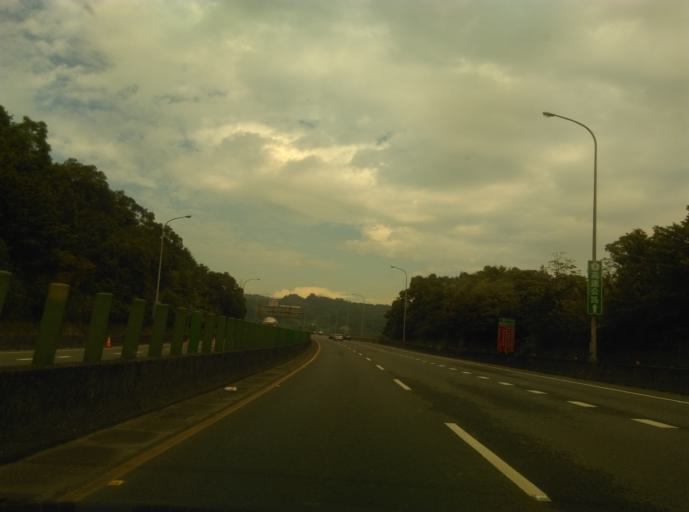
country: TW
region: Taiwan
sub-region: Keelung
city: Keelung
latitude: 25.1189
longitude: 121.6968
